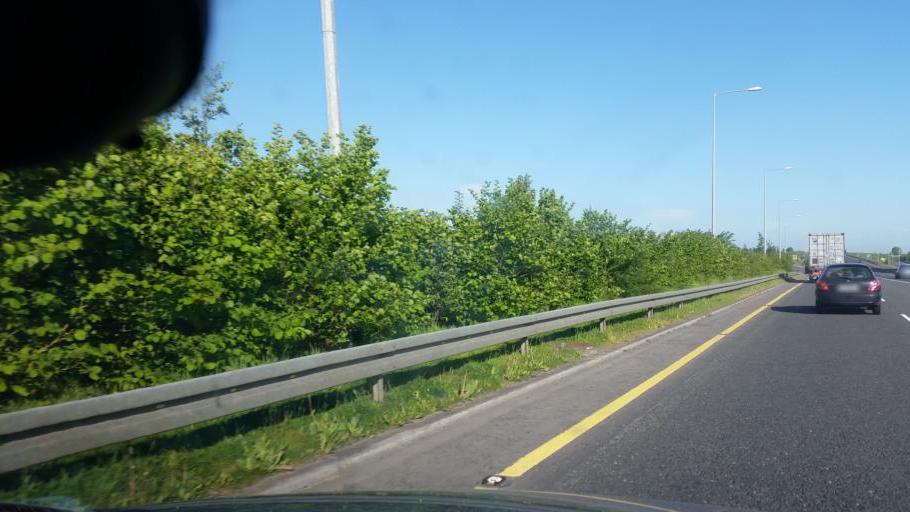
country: IE
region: Leinster
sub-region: Dublin City
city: Finglas
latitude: 53.4288
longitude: -6.3368
